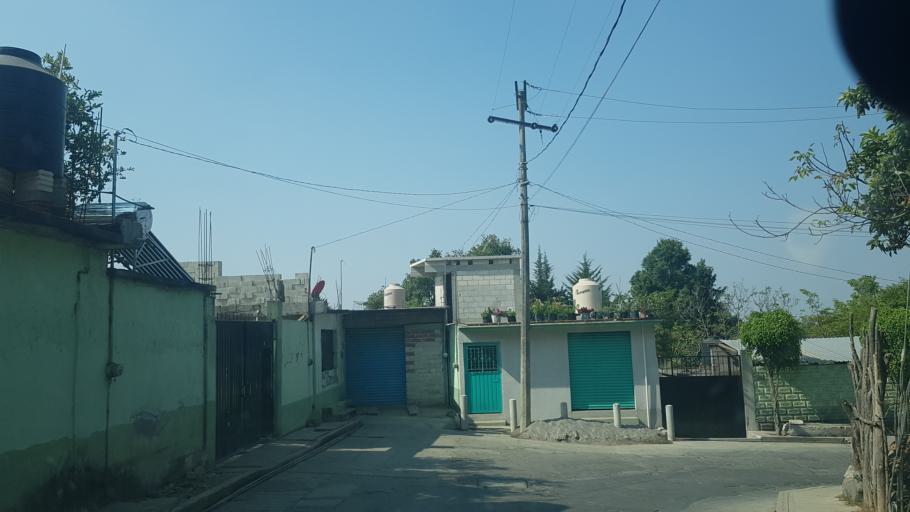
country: MX
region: Morelos
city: Hueyapan
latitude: 18.8835
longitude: -98.6897
